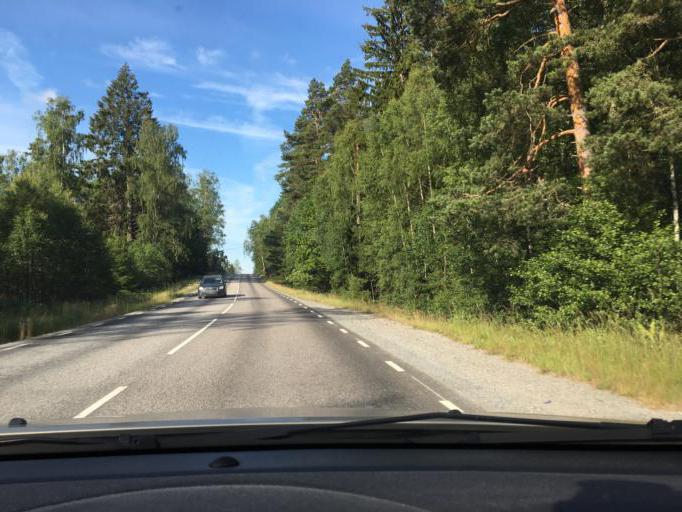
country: SE
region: Stockholm
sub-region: Salems Kommun
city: Ronninge
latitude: 59.2299
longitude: 17.6905
